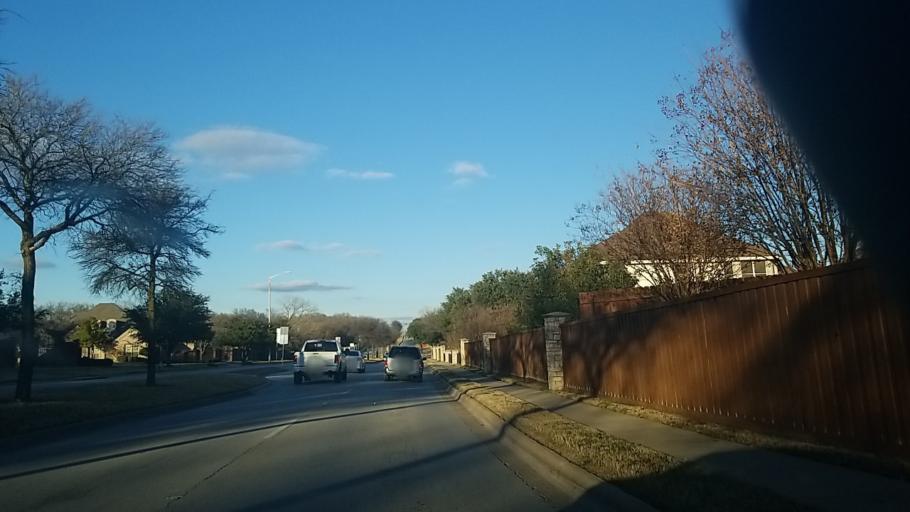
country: US
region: Texas
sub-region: Denton County
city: Denton
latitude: 33.1777
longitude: -97.1127
